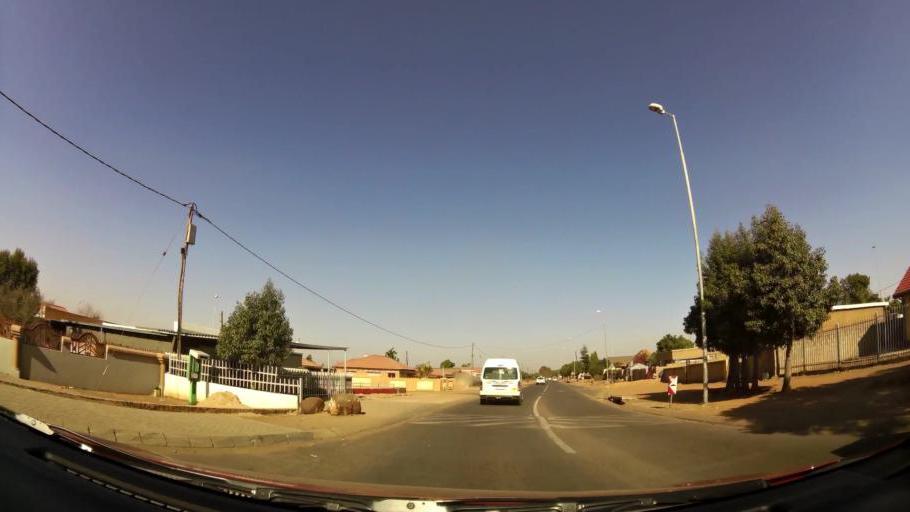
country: ZA
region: Gauteng
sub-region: City of Tshwane Metropolitan Municipality
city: Mabopane
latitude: -25.5334
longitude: 28.1042
